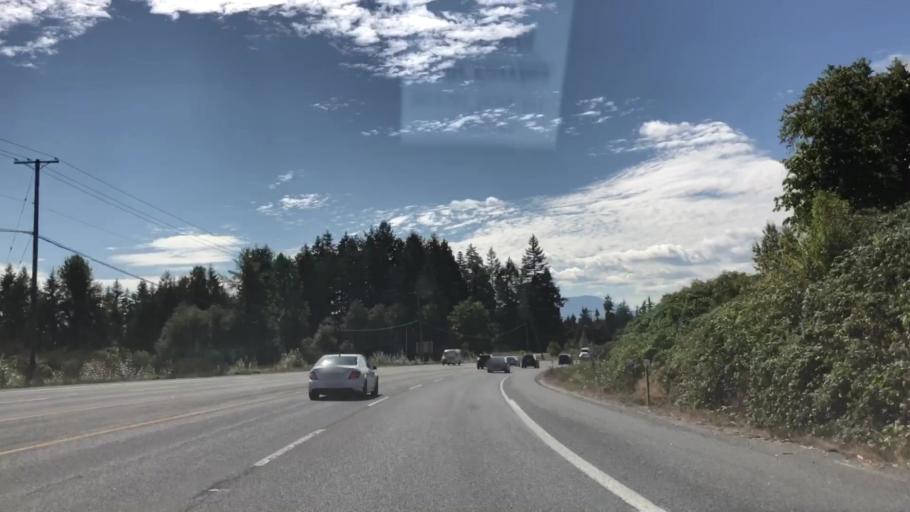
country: CA
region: British Columbia
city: Nanaimo
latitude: 49.1209
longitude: -123.8629
